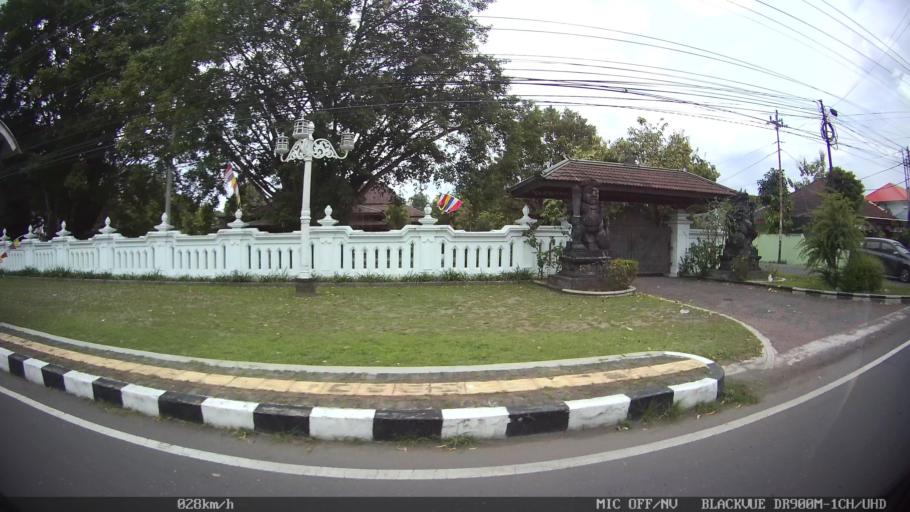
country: ID
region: Daerah Istimewa Yogyakarta
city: Yogyakarta
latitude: -7.7926
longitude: 110.3922
